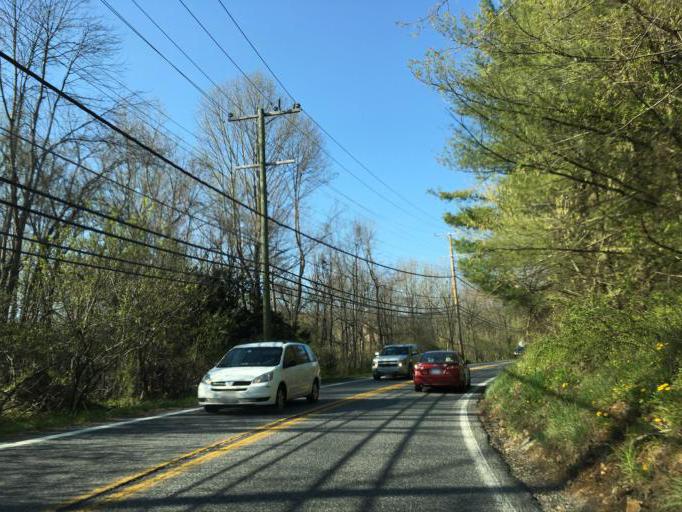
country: US
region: Maryland
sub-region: Baltimore County
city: Hunt Valley
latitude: 39.4960
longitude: -76.6426
